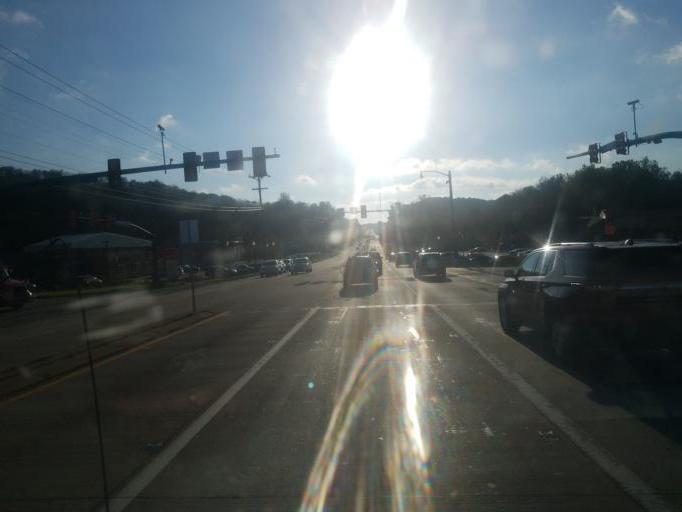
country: US
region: Pennsylvania
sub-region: Westmoreland County
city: Murrysville
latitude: 40.4226
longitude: -79.6620
